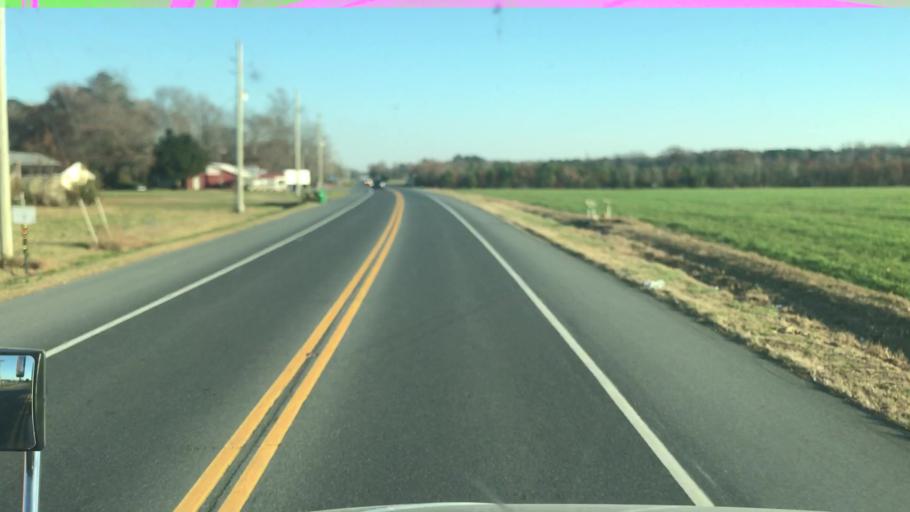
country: US
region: Delaware
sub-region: Sussex County
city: Bridgeville
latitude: 38.7855
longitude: -75.6793
